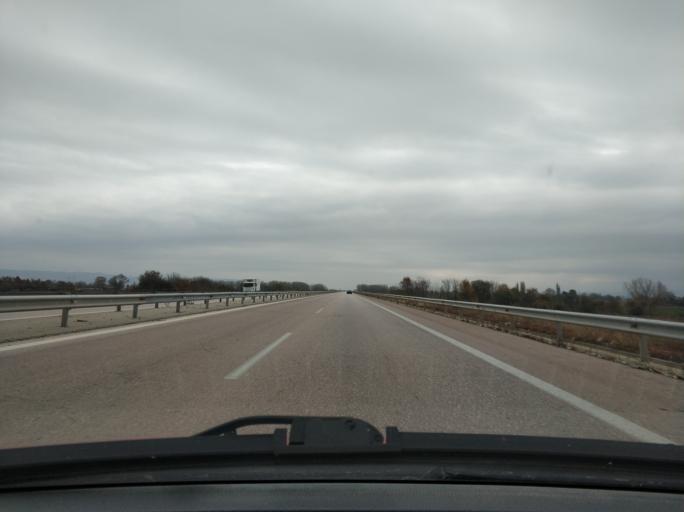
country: GR
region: Central Macedonia
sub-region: Nomos Thessalonikis
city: Kavallari
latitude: 40.7327
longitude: 23.0480
